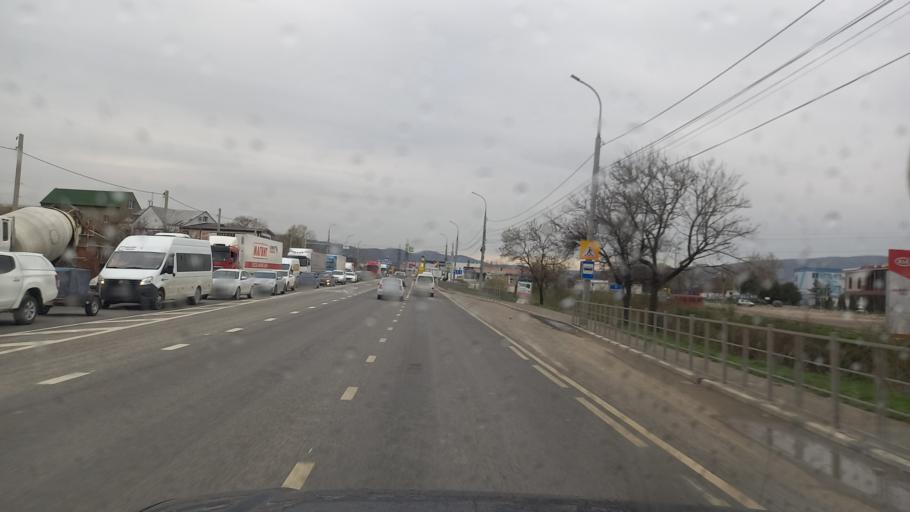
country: RU
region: Krasnodarskiy
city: Gayduk
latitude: 44.7650
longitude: 37.7147
